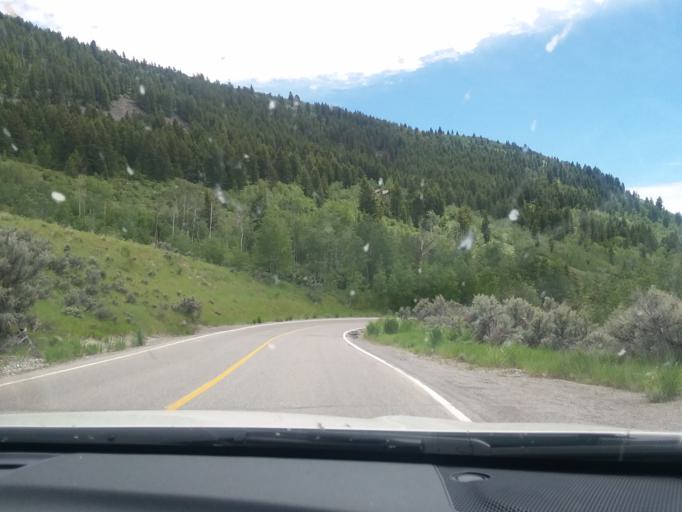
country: US
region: Wyoming
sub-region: Teton County
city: Jackson
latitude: 43.4928
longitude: -110.7873
